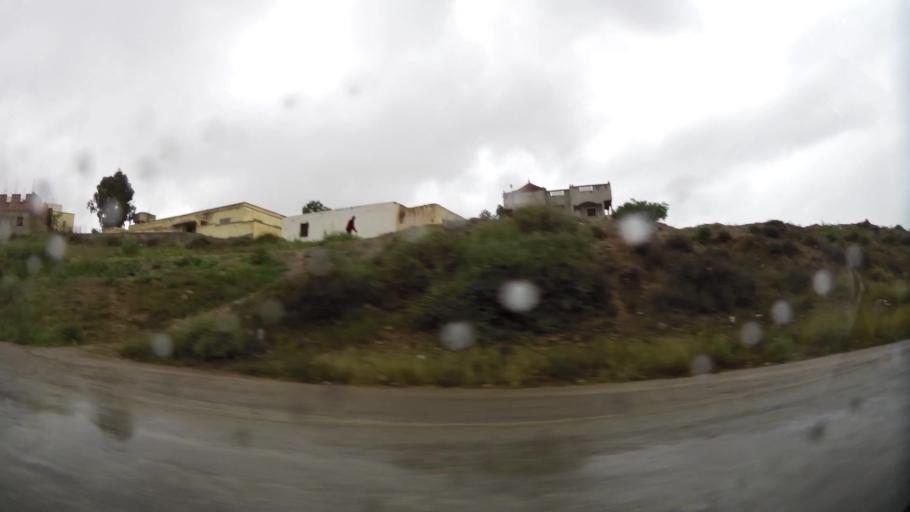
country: MA
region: Oriental
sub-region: Nador
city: Midar
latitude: 34.8917
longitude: -3.7418
